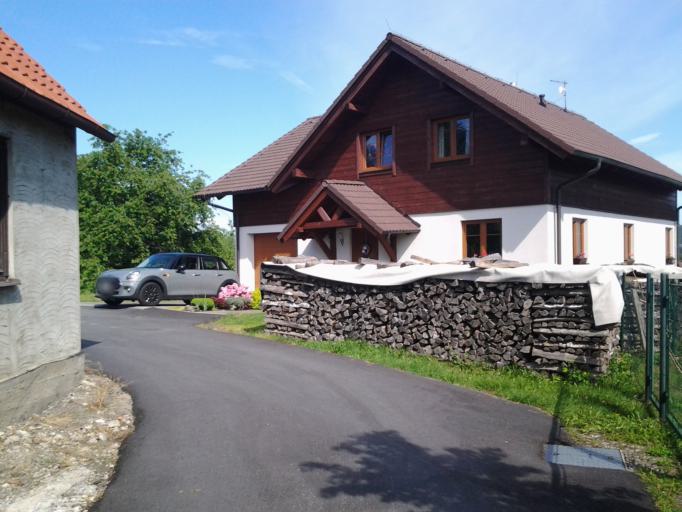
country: CZ
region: Jihocesky
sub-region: Okres Cesky Krumlov
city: Cesky Krumlov
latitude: 48.8195
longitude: 14.3091
